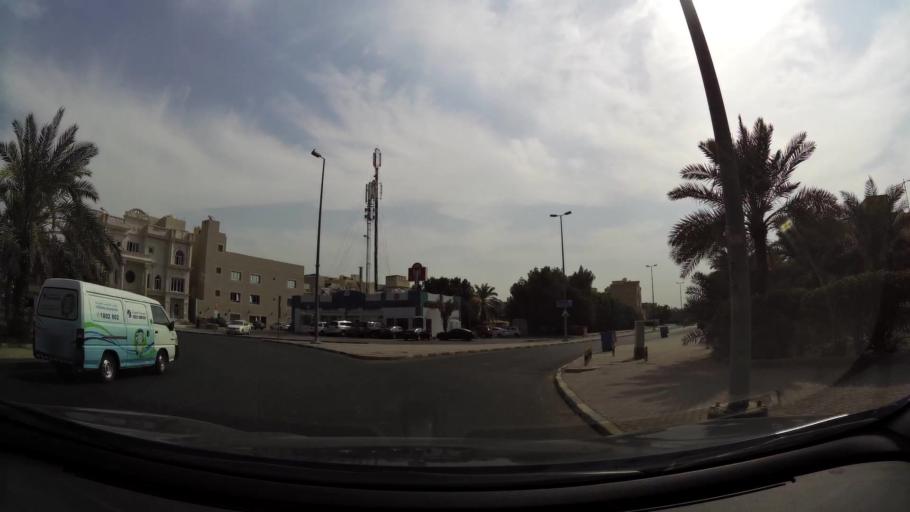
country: KW
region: Al Asimah
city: Ash Shamiyah
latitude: 29.3498
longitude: 47.9633
